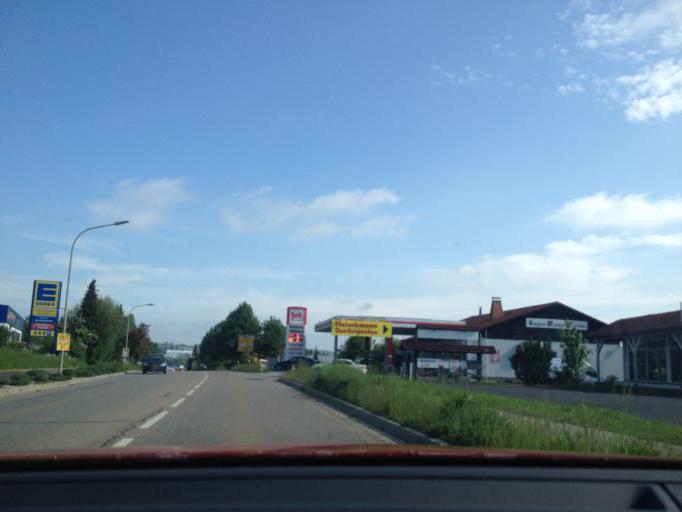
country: DE
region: Bavaria
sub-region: Upper Palatinate
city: Waldershof
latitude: 49.9829
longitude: 12.0683
